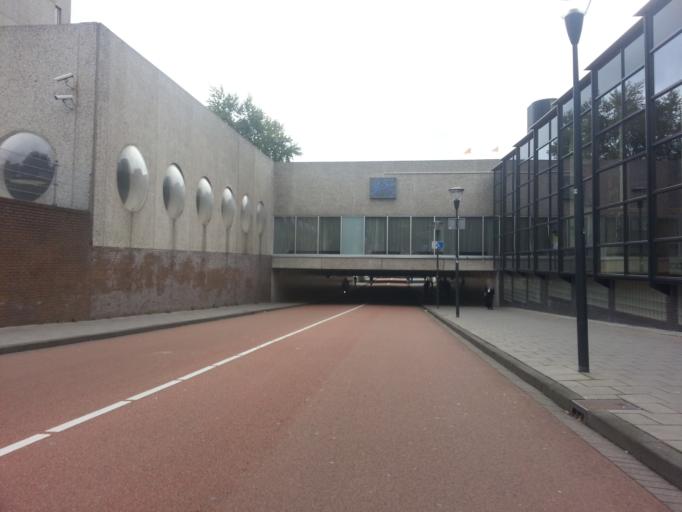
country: NL
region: North Brabant
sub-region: Gemeente Eindhoven
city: Eindhoven
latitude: 51.4450
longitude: 5.4750
